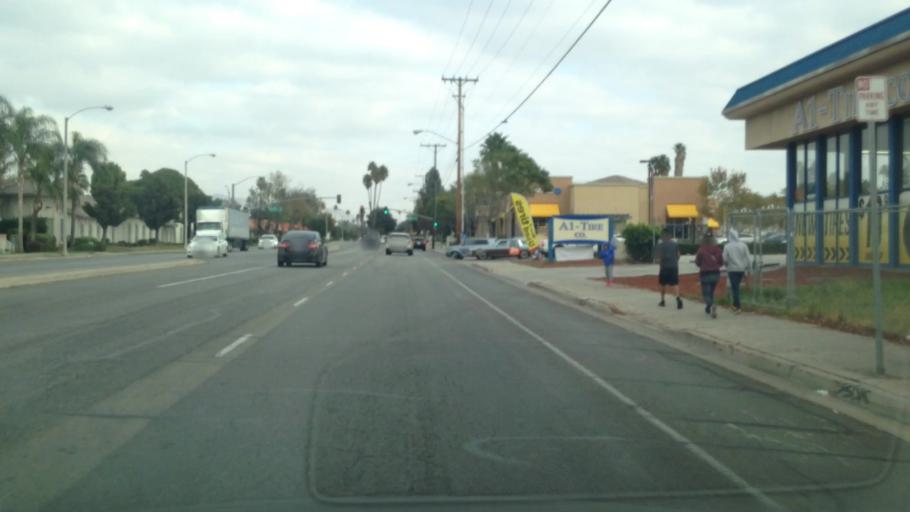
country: US
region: California
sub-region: Riverside County
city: Riverside
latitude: 33.9460
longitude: -117.4148
